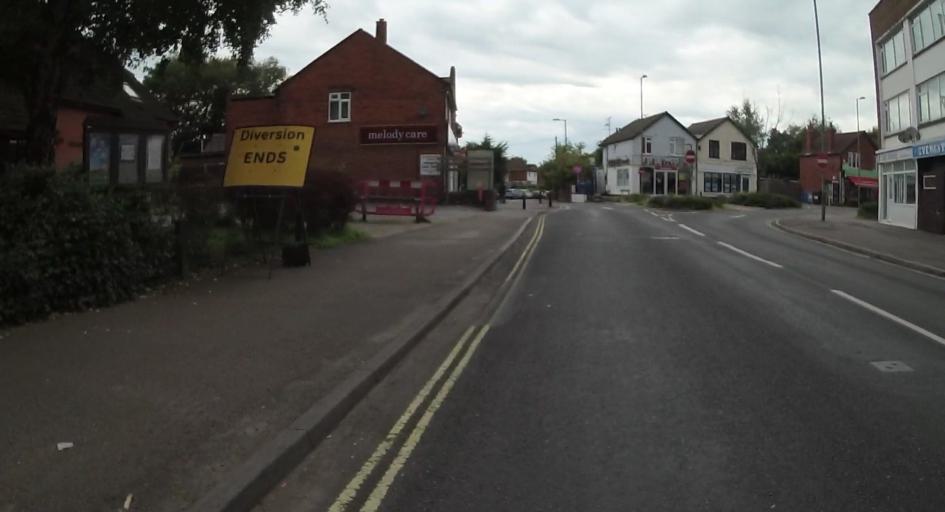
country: GB
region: England
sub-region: Hampshire
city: Farnborough
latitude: 51.2917
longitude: -0.7694
